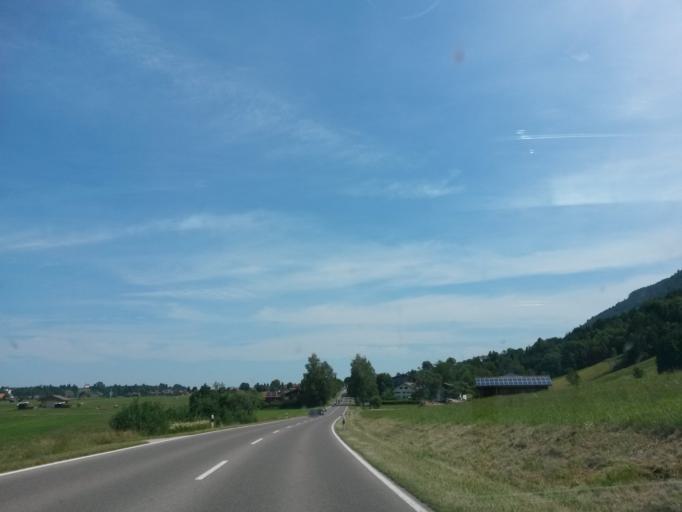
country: DE
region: Bavaria
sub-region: Swabia
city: Halblech
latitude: 47.6090
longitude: 10.7994
